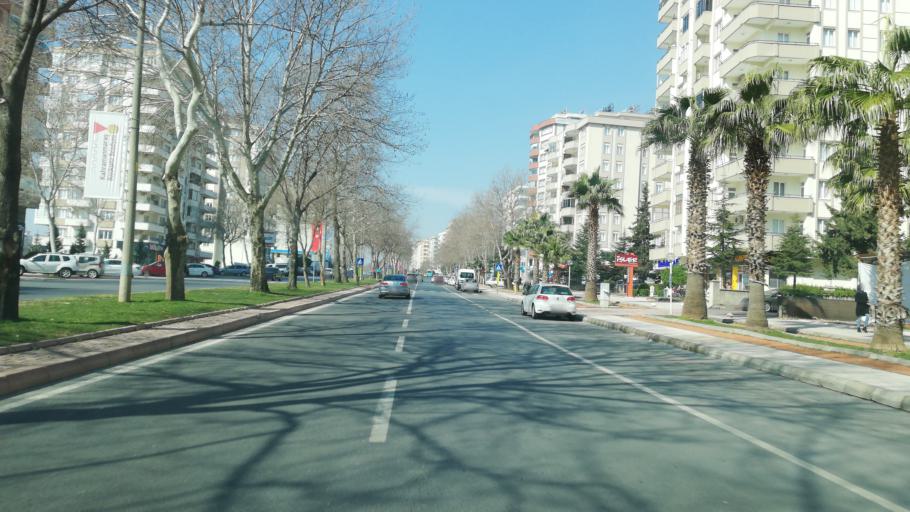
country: TR
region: Kahramanmaras
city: Kahramanmaras
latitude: 37.5878
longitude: 36.8911
